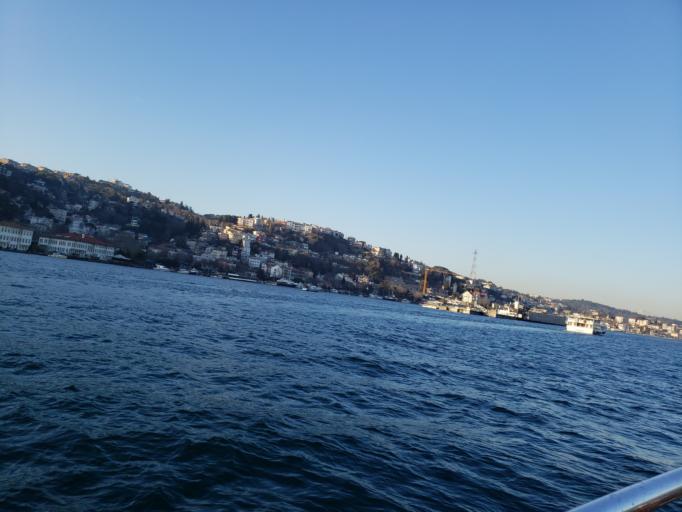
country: TR
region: Istanbul
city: UEskuedar
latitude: 41.0563
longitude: 29.0393
